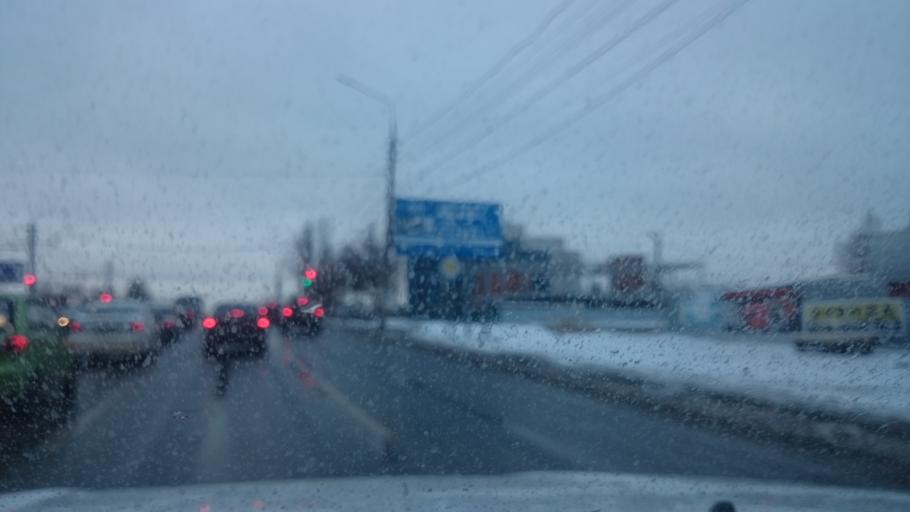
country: RU
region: Tula
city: Mendeleyevskiy
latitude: 54.1449
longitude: 37.5820
